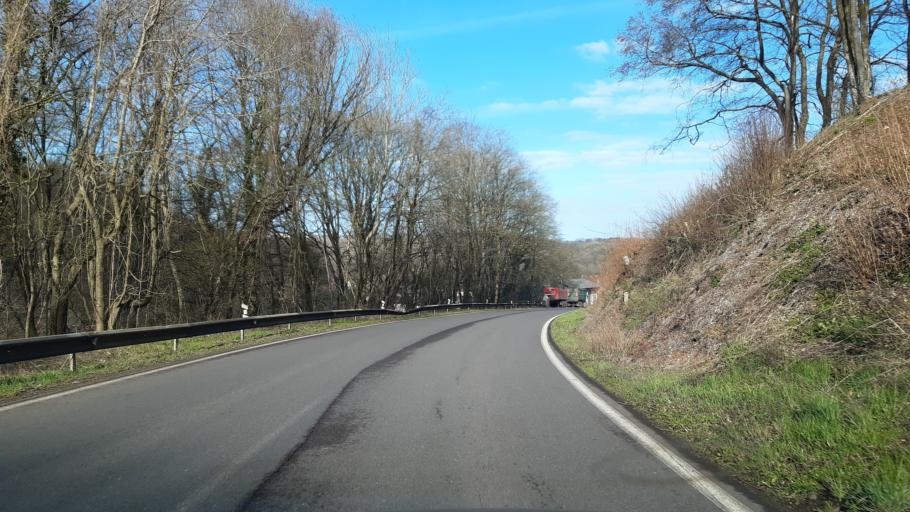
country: FR
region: Lorraine
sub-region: Departement de la Moselle
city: Audun-le-Tiche
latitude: 49.4644
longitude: 5.9617
